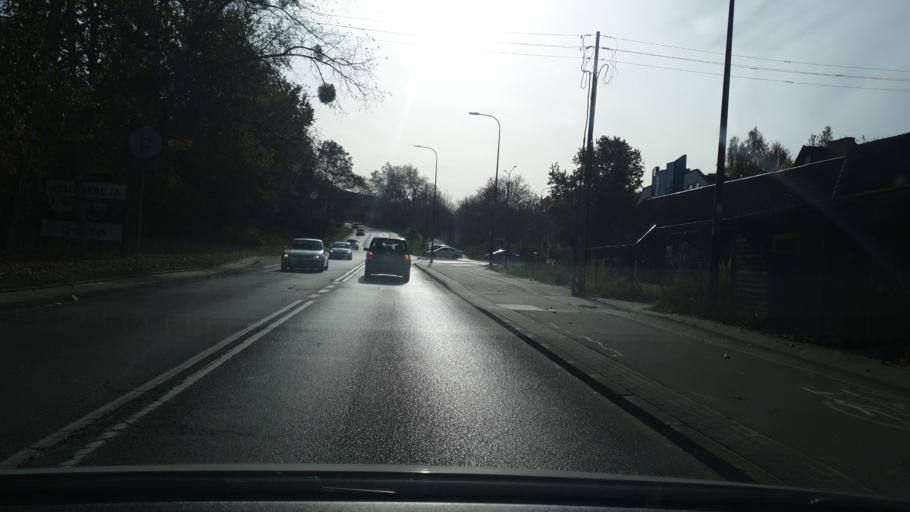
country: PL
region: Pomeranian Voivodeship
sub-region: Gdansk
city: Gdansk
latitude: 54.3649
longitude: 18.5890
